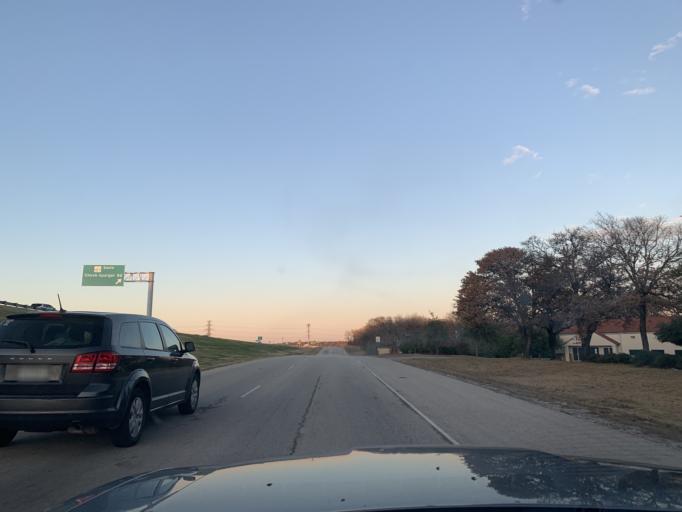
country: US
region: Texas
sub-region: Tarrant County
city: Euless
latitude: 32.8595
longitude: -97.1046
